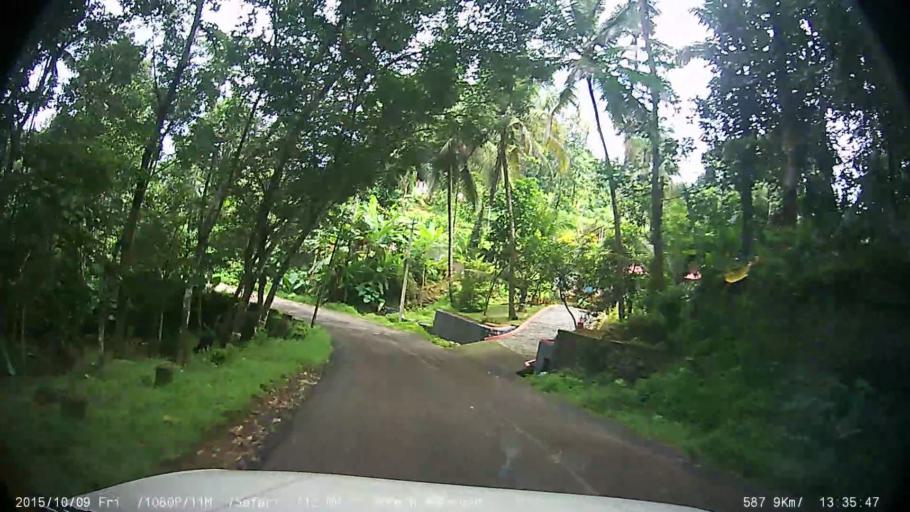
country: IN
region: Kerala
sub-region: Ernakulam
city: Piravam
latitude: 9.8997
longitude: 76.5598
